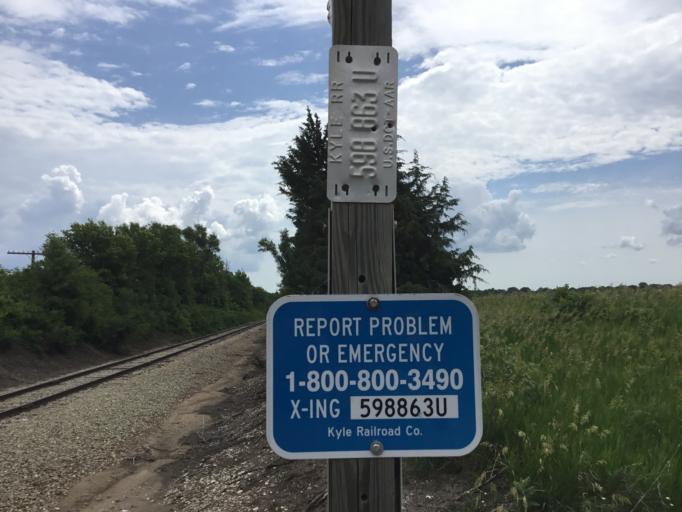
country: US
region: Kansas
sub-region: Republic County
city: Belleville
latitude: 39.8257
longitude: -97.6520
